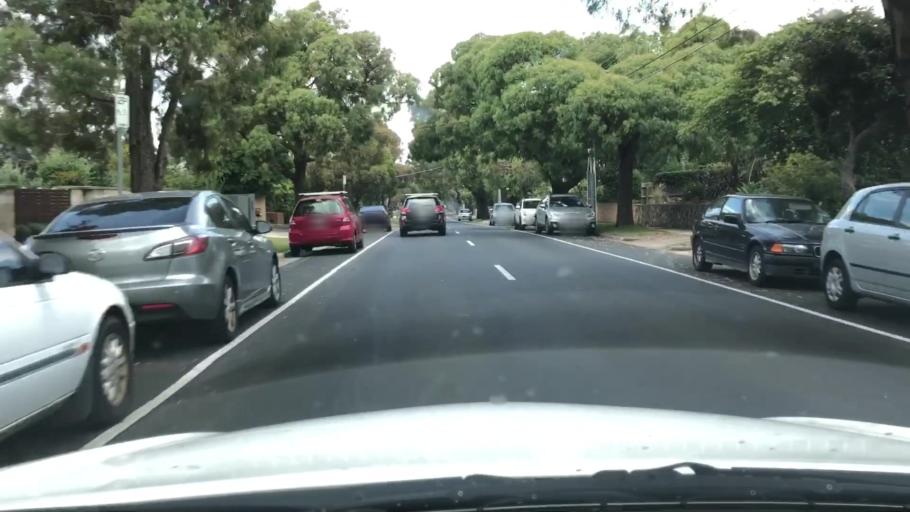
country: AU
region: Victoria
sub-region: Bayside
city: Black Rock
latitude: -37.9623
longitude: 145.0210
